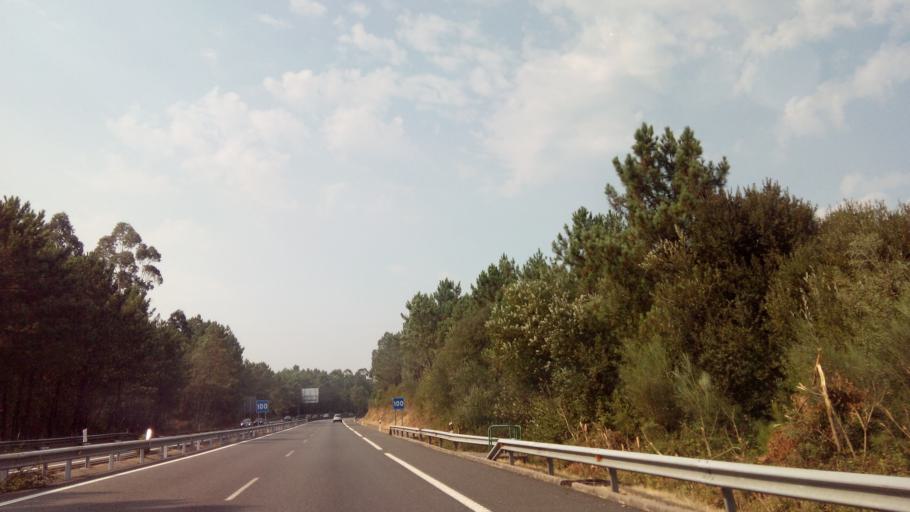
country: ES
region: Galicia
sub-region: Provincia de Pontevedra
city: Tui
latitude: 42.0749
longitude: -8.6323
